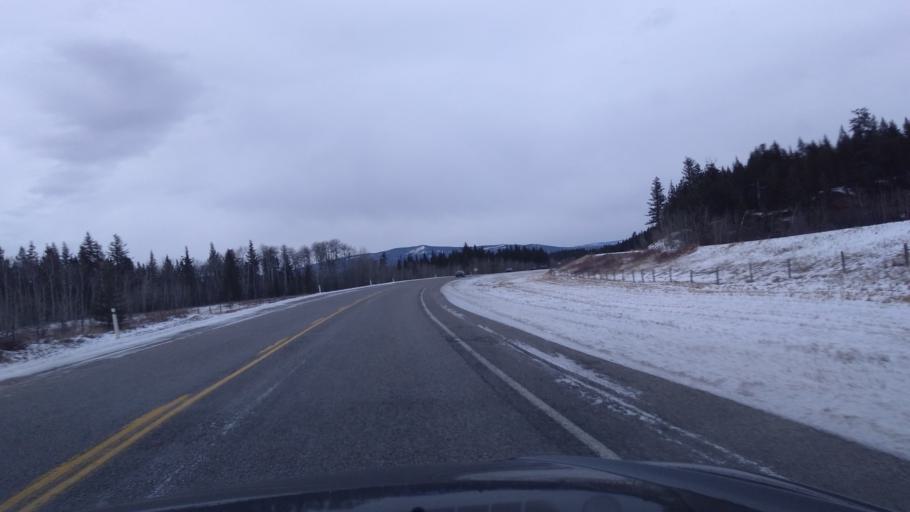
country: CA
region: Alberta
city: Canmore
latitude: 51.0804
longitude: -115.0115
